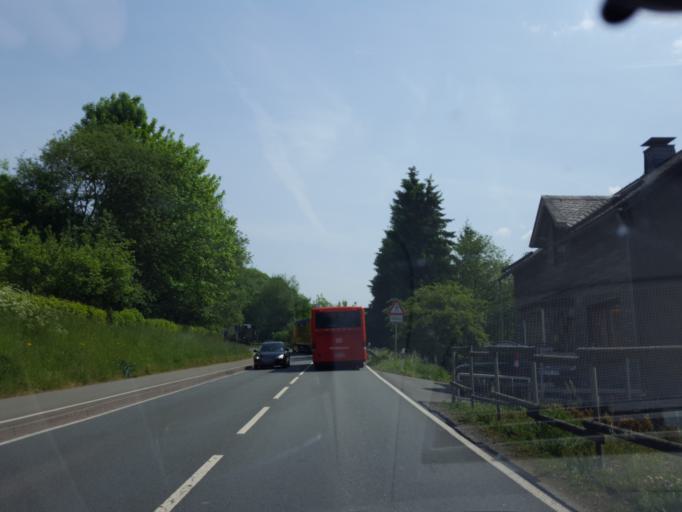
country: DE
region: North Rhine-Westphalia
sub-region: Regierungsbezirk Arnsberg
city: Olsberg
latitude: 51.3694
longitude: 8.4635
